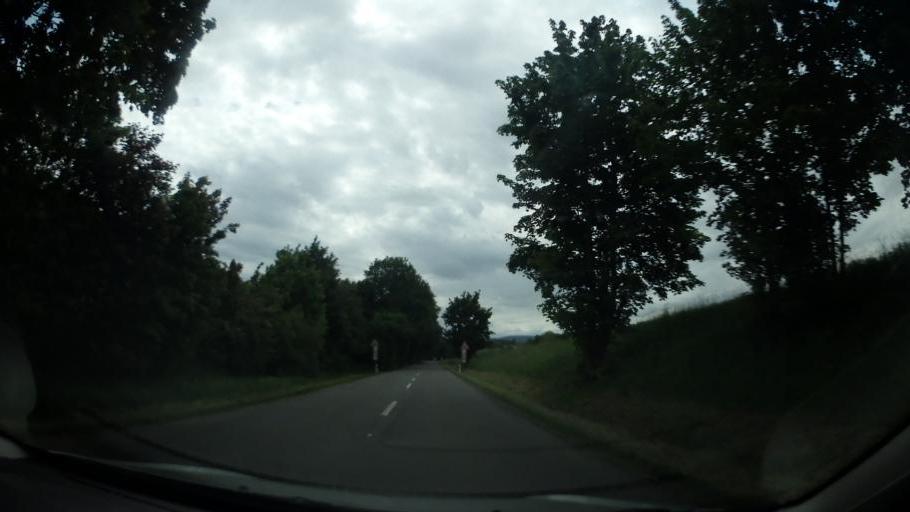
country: CZ
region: Pardubicky
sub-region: Okres Svitavy
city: Moravska Trebova
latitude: 49.7814
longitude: 16.6671
